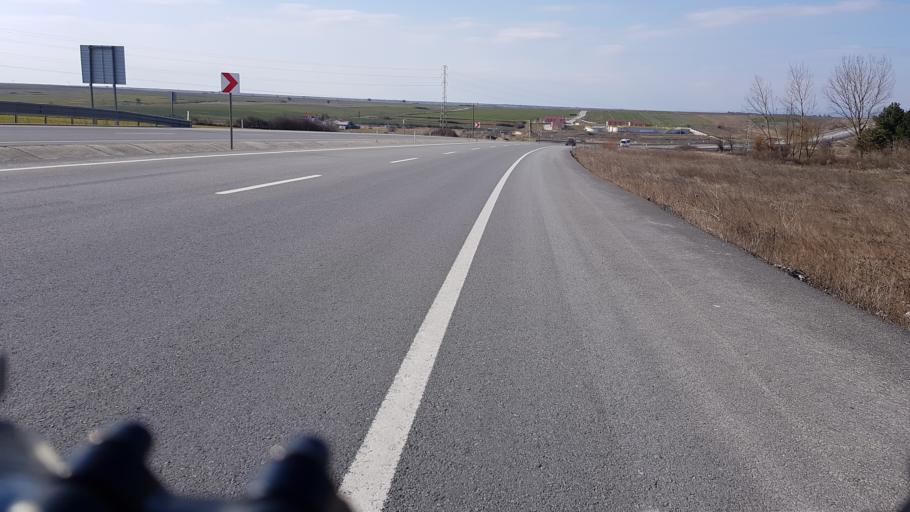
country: TR
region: Tekirdag
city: Saray
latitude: 41.4216
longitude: 27.9162
